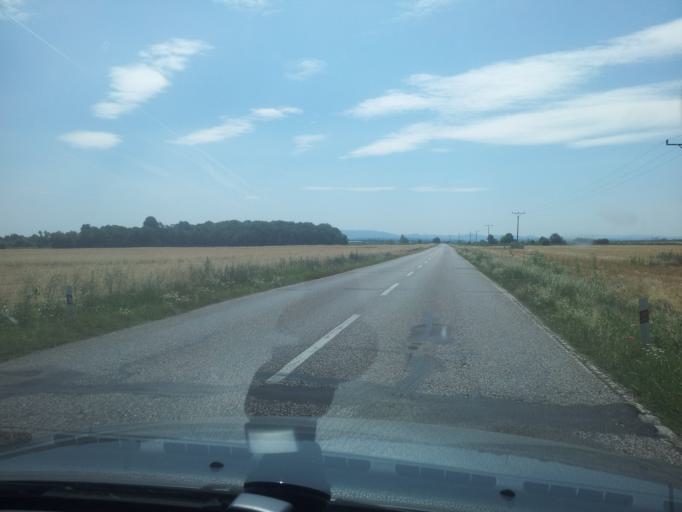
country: SK
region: Nitriansky
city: Levice
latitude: 48.1268
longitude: 18.5991
